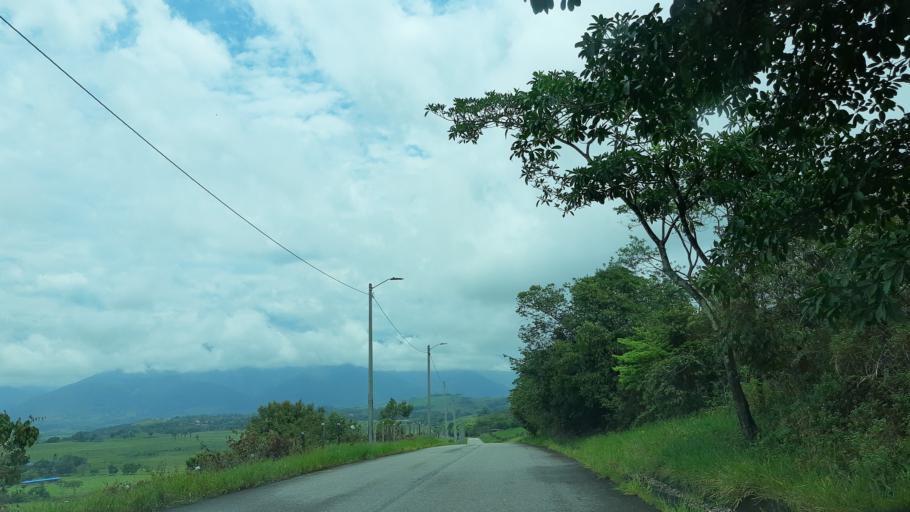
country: CO
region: Casanare
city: Sabanalarga
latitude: 4.8323
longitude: -73.0459
